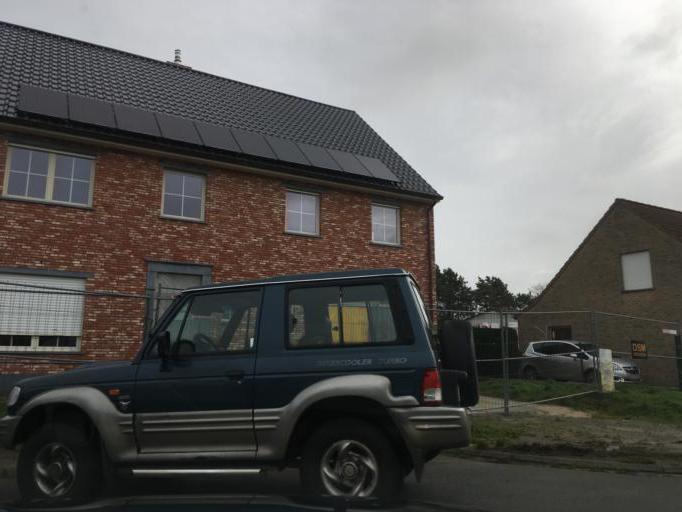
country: BE
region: Flanders
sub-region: Provincie West-Vlaanderen
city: Roeselare
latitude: 50.9657
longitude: 3.1233
